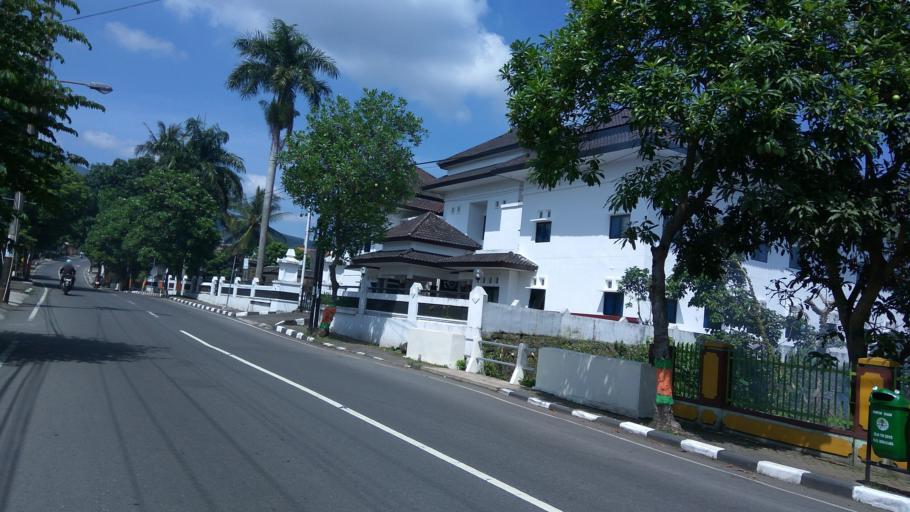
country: ID
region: Central Java
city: Ungaran
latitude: -7.1369
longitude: 110.4087
